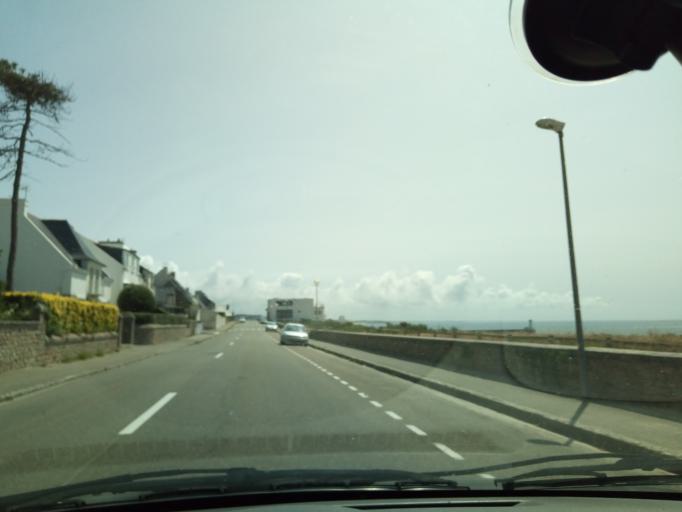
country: FR
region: Brittany
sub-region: Departement du Finistere
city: Audierne
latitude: 48.0124
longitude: -4.5456
